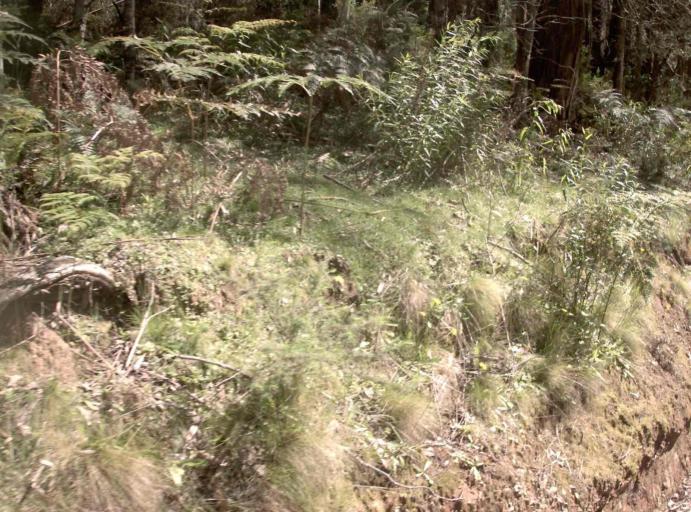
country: AU
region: New South Wales
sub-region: Bombala
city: Bombala
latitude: -37.0690
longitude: 148.7881
